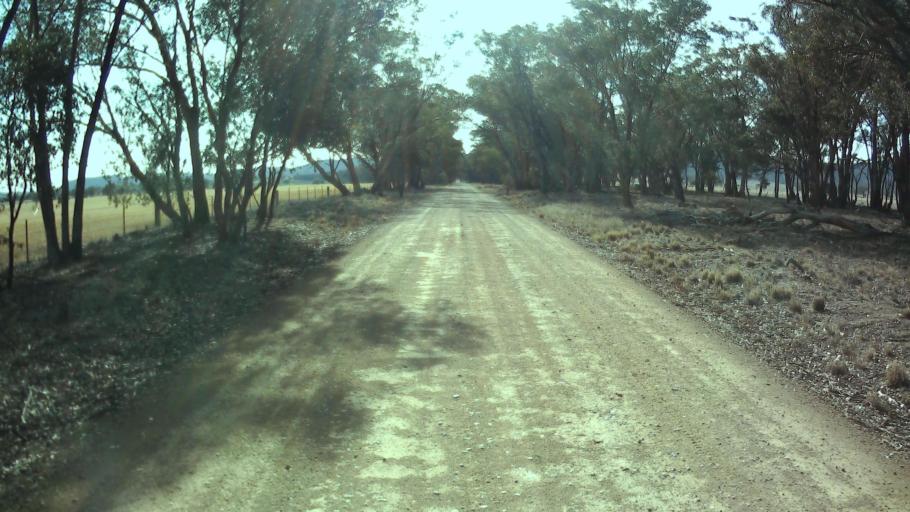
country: AU
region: New South Wales
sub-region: Weddin
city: Grenfell
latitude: -33.7968
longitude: 148.0849
